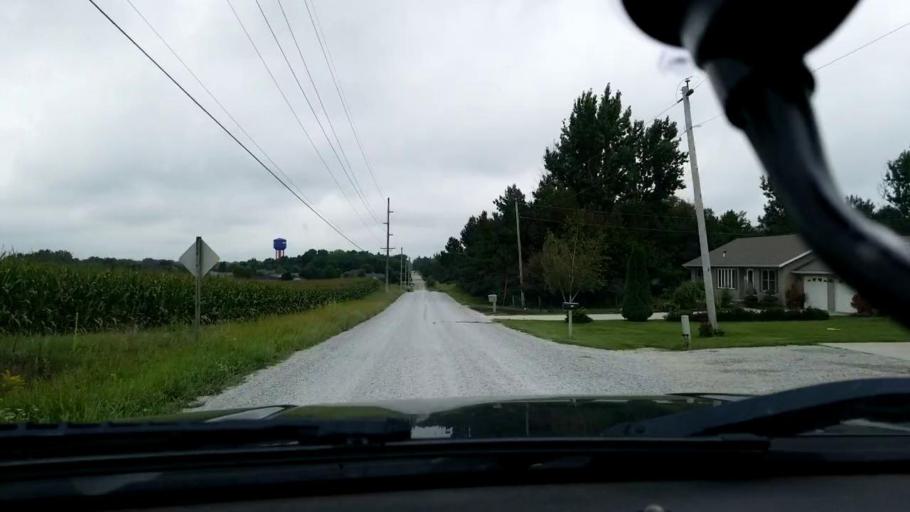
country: US
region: Iowa
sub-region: Buchanan County
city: Independence
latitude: 42.4880
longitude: -91.8845
